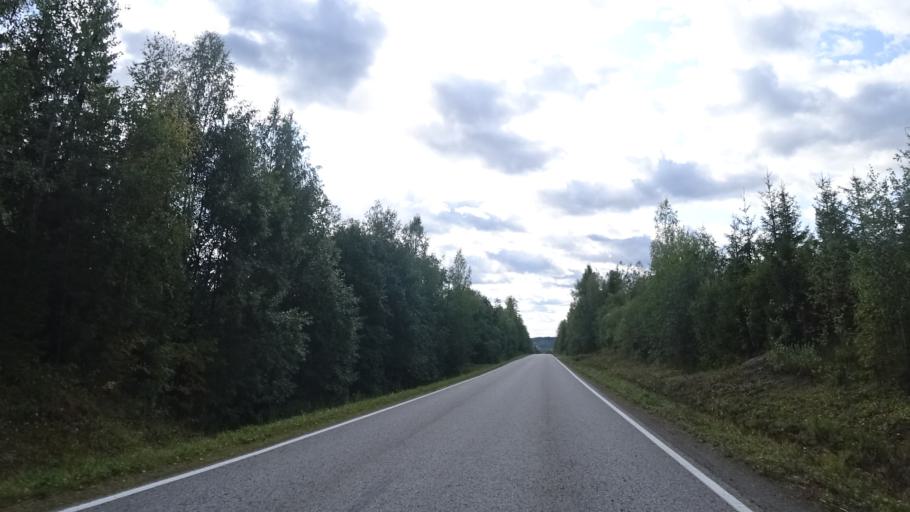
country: RU
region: Republic of Karelia
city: Vyartsilya
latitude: 62.2242
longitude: 30.6565
